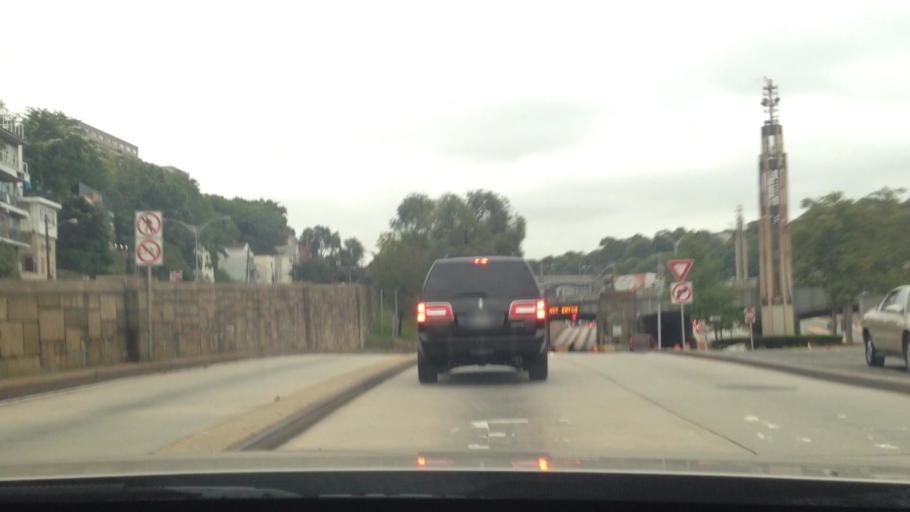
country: US
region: New Jersey
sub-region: Hudson County
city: Weehawken
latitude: 40.7624
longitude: -74.0258
